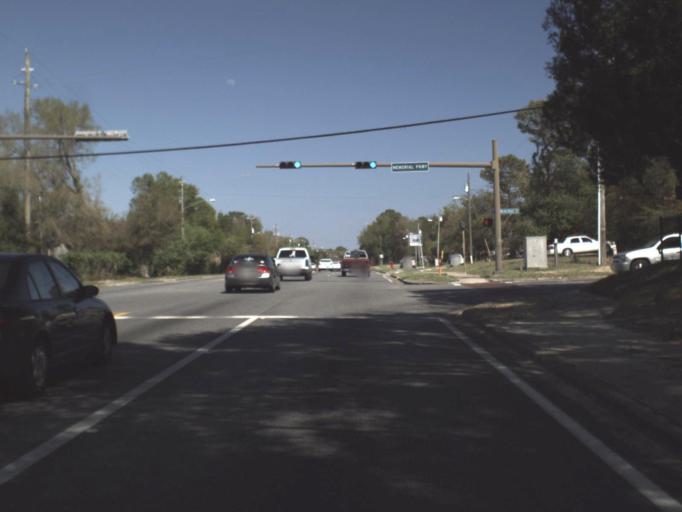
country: US
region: Florida
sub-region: Okaloosa County
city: Ocean City
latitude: 30.4272
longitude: -86.6309
